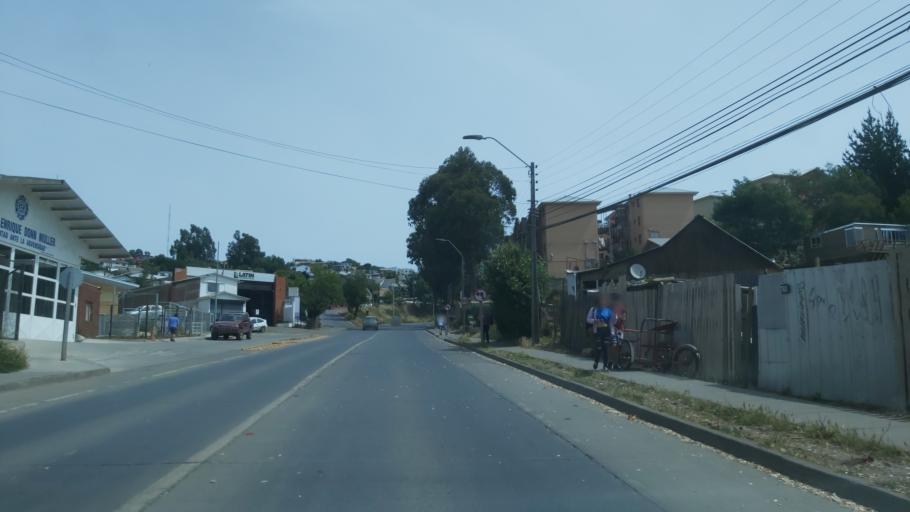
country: CL
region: Maule
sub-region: Provincia de Talca
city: Constitucion
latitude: -35.3358
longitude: -72.4167
